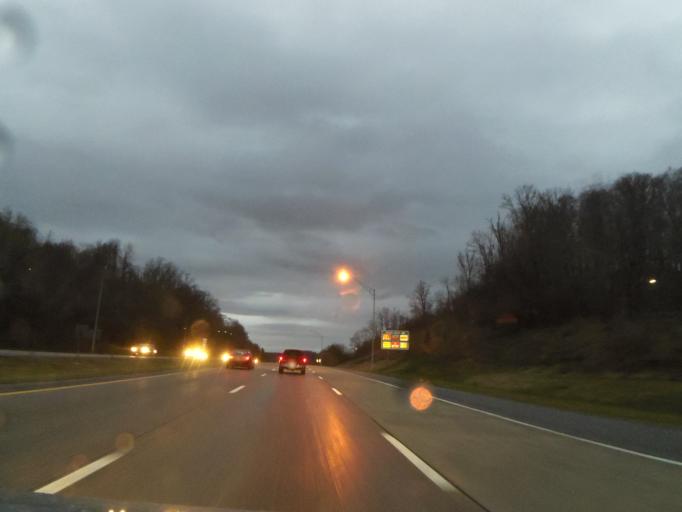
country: US
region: Tennessee
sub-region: Washington County
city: Oak Grove
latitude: 36.3607
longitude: -82.4053
